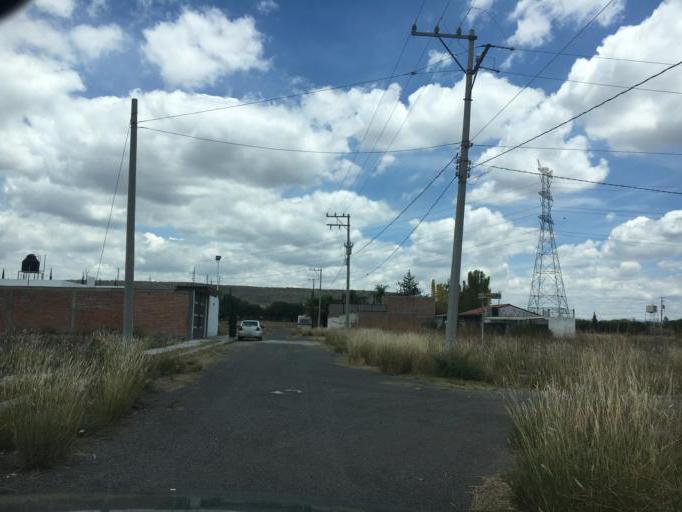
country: MX
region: Guanajuato
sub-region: San Francisco del Rincon
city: Barrio de Guadalupe del Mezquitillo
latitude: 20.9263
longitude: -101.7516
